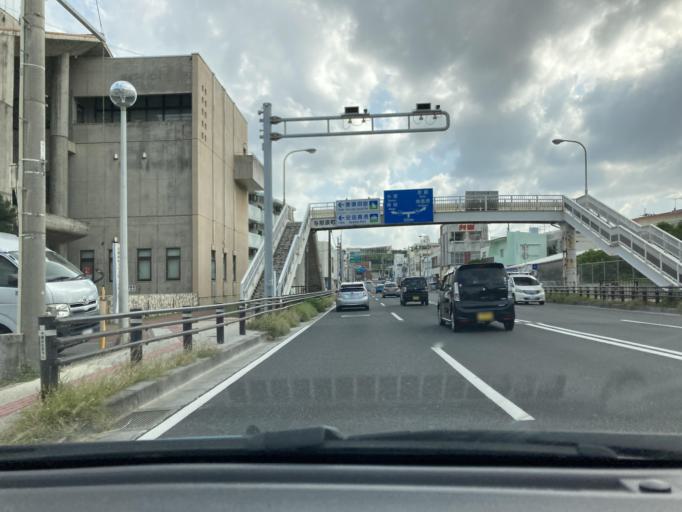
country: JP
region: Okinawa
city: Ginowan
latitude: 26.2040
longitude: 127.7553
